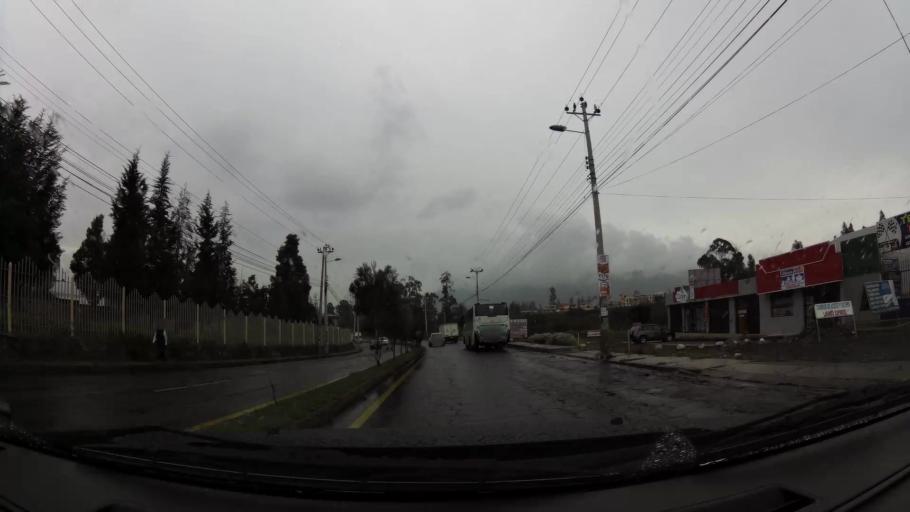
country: EC
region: Pichincha
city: Sangolqui
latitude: -0.3125
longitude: -78.4418
